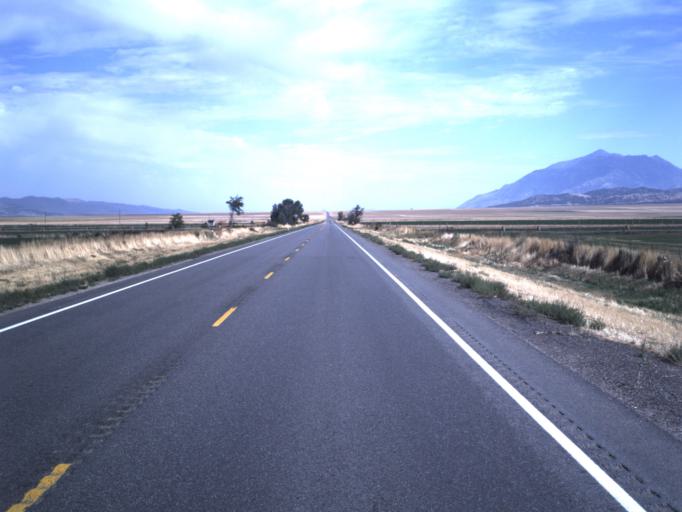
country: US
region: Utah
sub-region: Juab County
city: Nephi
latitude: 39.5667
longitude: -111.8619
